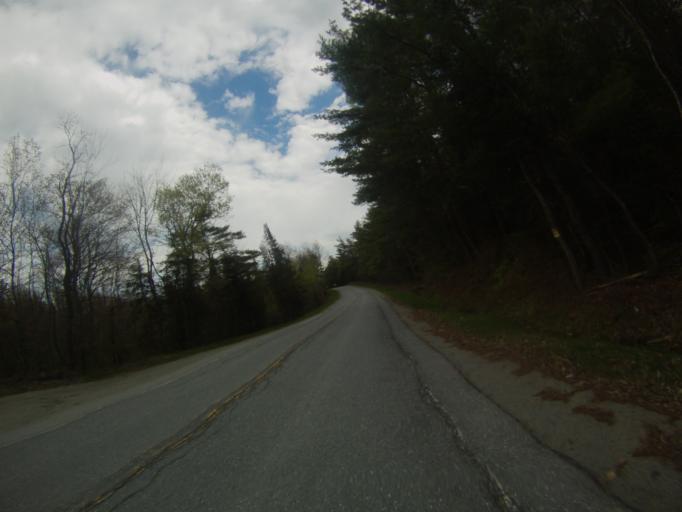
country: US
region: New York
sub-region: Essex County
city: Mineville
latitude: 44.0962
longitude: -73.5543
